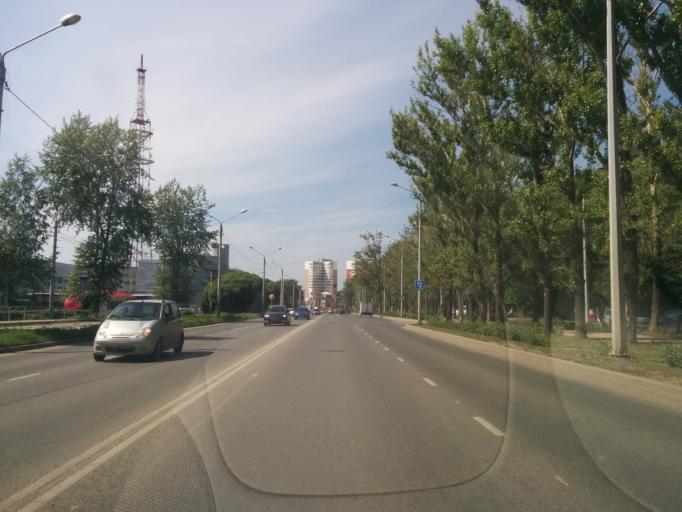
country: RU
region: Perm
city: Perm
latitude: 57.9917
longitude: 56.2938
